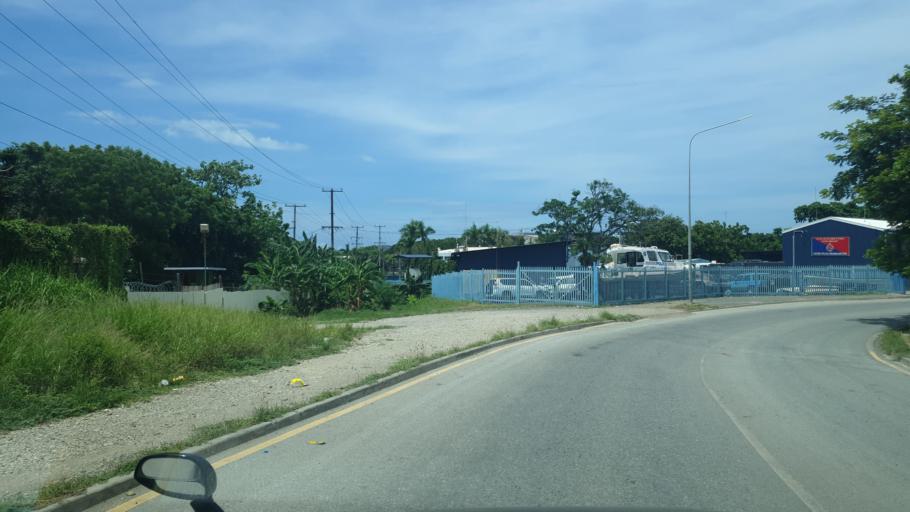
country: PG
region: National Capital
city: Port Moresby
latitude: -9.4636
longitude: 147.1605
